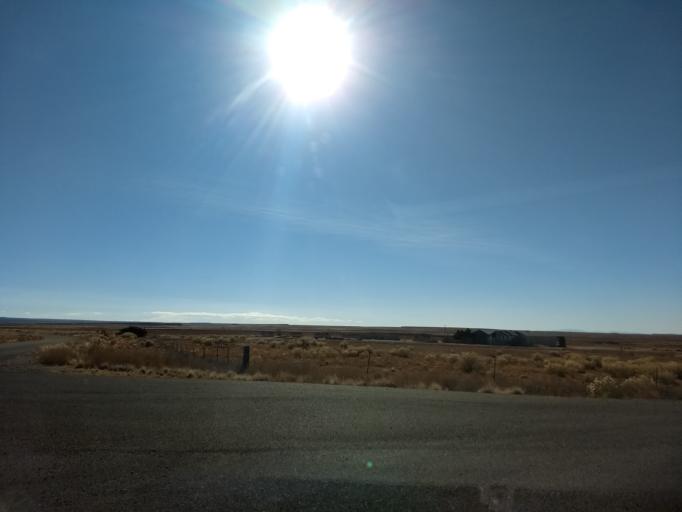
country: US
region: Arizona
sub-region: Coconino County
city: Fredonia
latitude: 36.9319
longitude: -112.5045
